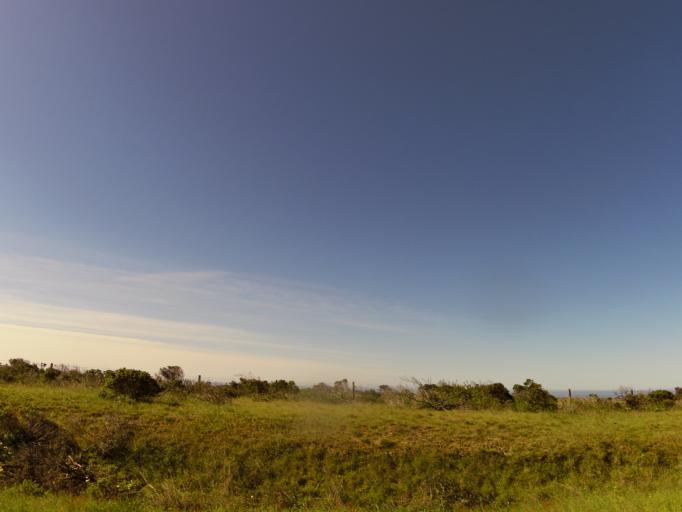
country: US
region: California
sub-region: Santa Cruz County
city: Bonny Doon
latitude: 37.1448
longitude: -122.3338
